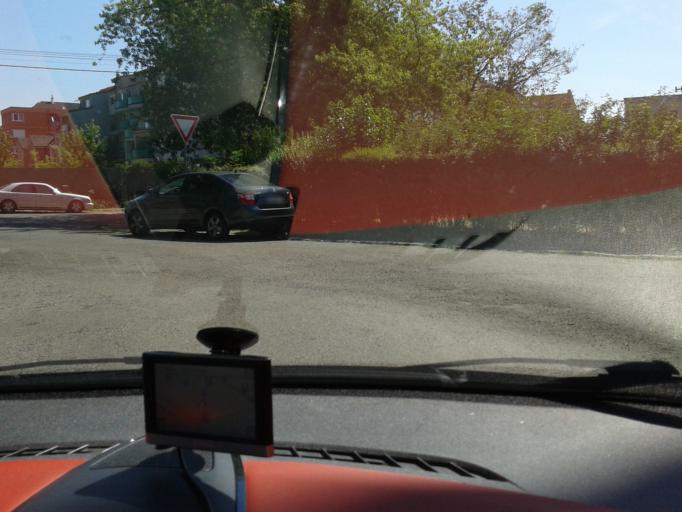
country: SK
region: Bratislavsky
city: Bratislava
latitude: 48.1682
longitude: 17.1623
